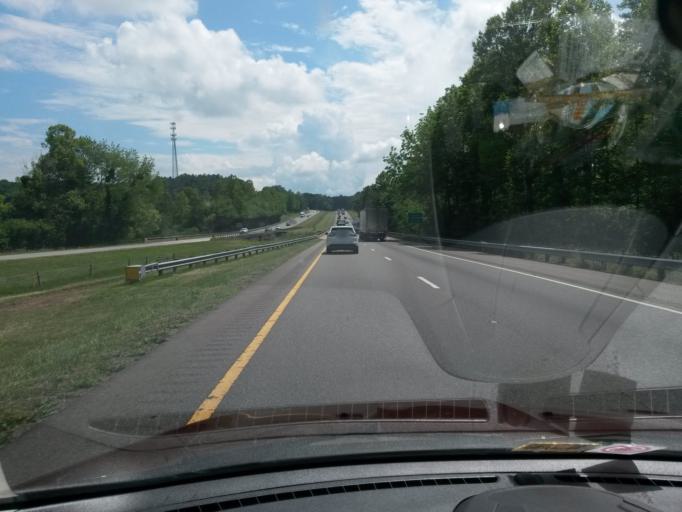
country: US
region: North Carolina
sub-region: Surry County
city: Dobson
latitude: 36.4472
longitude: -80.7746
